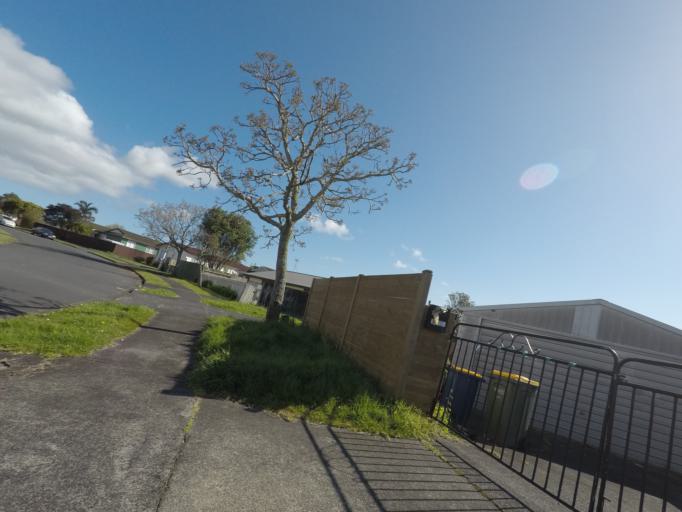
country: NZ
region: Auckland
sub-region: Auckland
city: Rosebank
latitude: -36.8603
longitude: 174.6020
